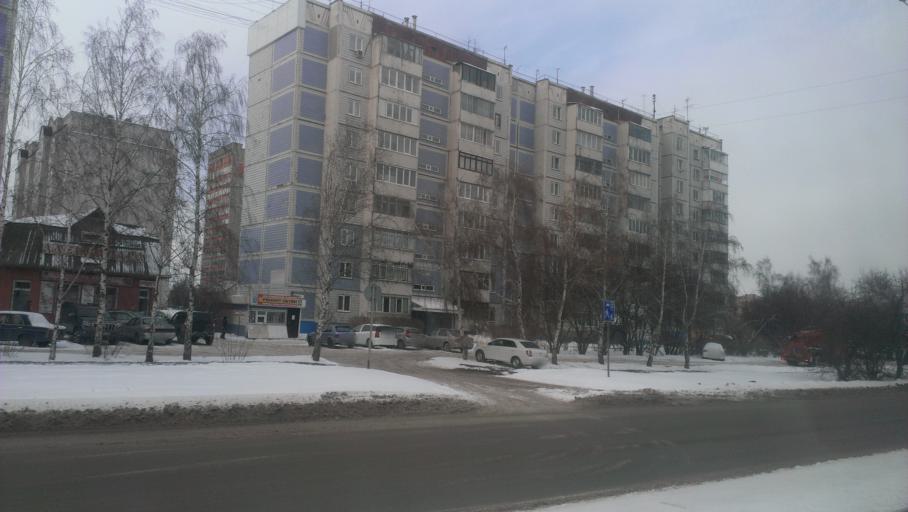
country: RU
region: Altai Krai
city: Novosilikatnyy
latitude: 53.3430
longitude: 83.6708
